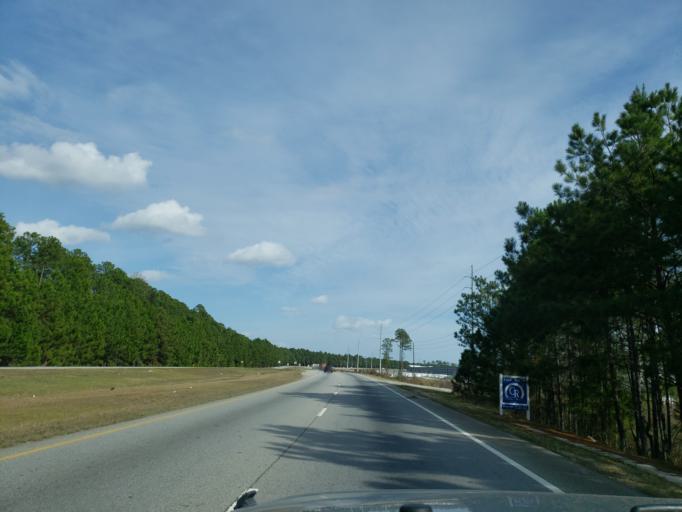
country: US
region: Georgia
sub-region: Chatham County
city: Pooler
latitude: 32.1650
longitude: -81.2278
